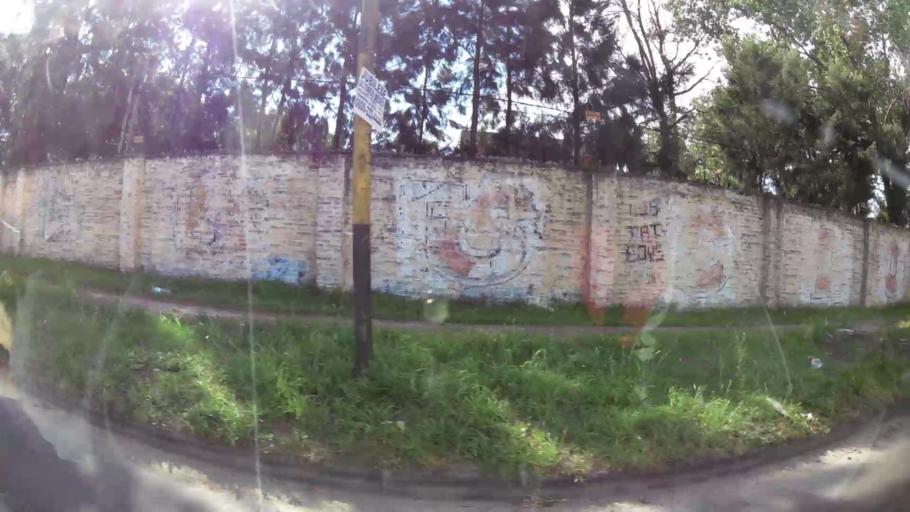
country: AR
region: Buenos Aires
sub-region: Partido de Merlo
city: Merlo
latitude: -34.6386
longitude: -58.7146
